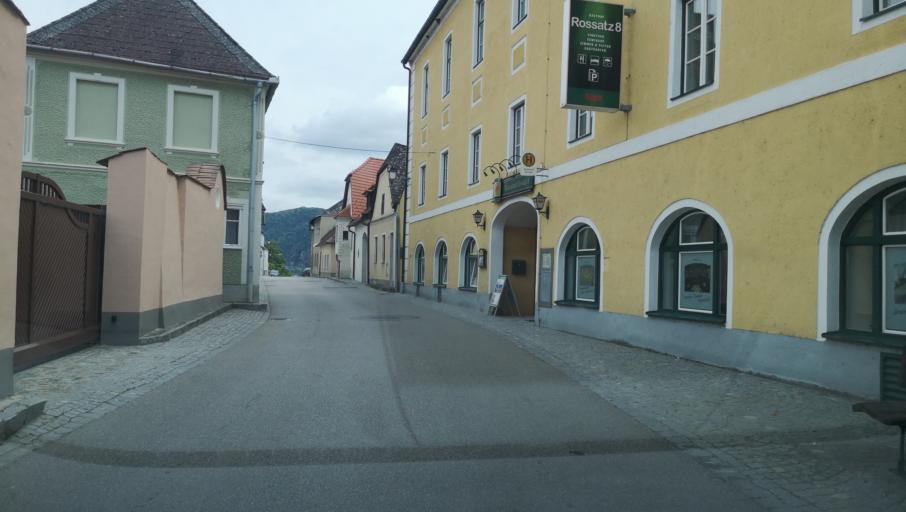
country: AT
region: Lower Austria
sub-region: Politischer Bezirk Krems
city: Durnstein
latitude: 48.3959
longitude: 15.5055
